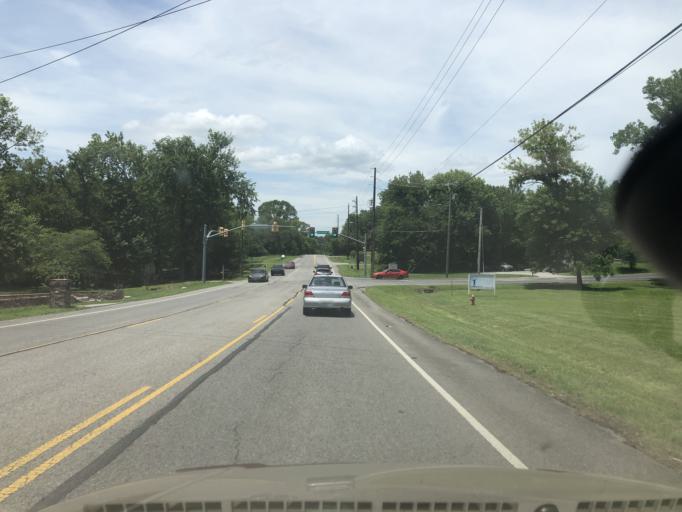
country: US
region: Tennessee
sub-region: Davidson County
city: Lakewood
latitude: 36.2493
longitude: -86.6859
